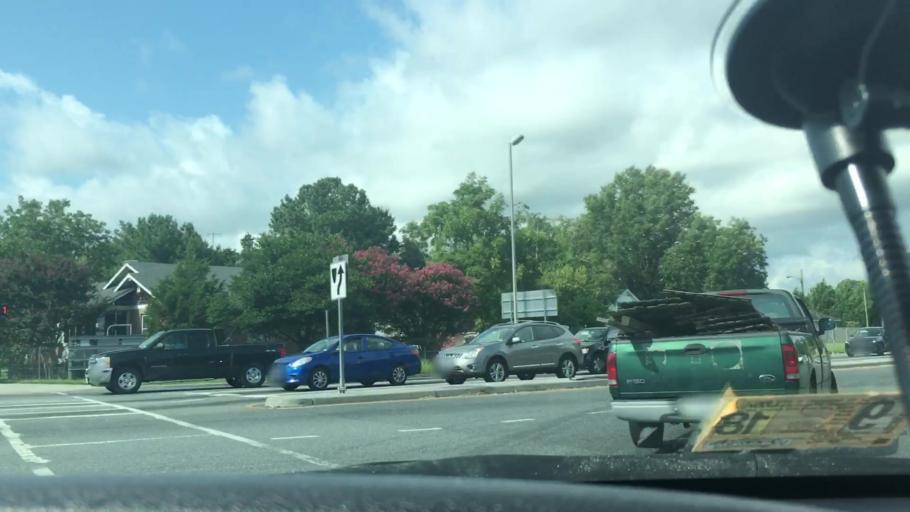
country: US
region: Virginia
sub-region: City of Virginia Beach
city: Virginia Beach
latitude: 36.8386
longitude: -76.0496
